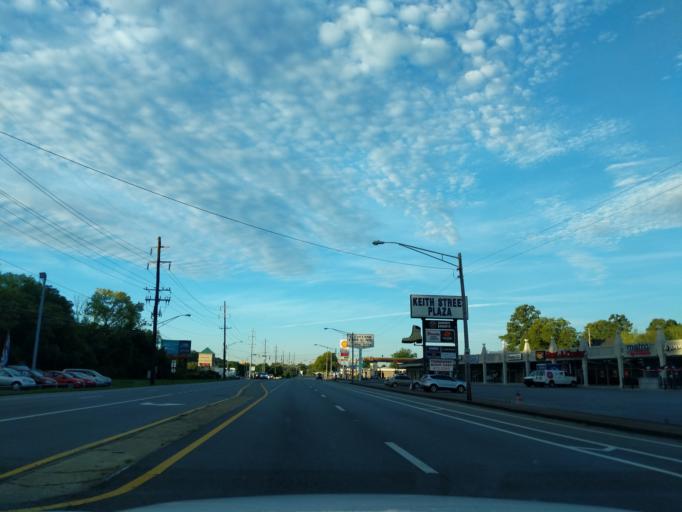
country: US
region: Tennessee
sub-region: Bradley County
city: Cleveland
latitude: 35.1645
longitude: -84.8823
